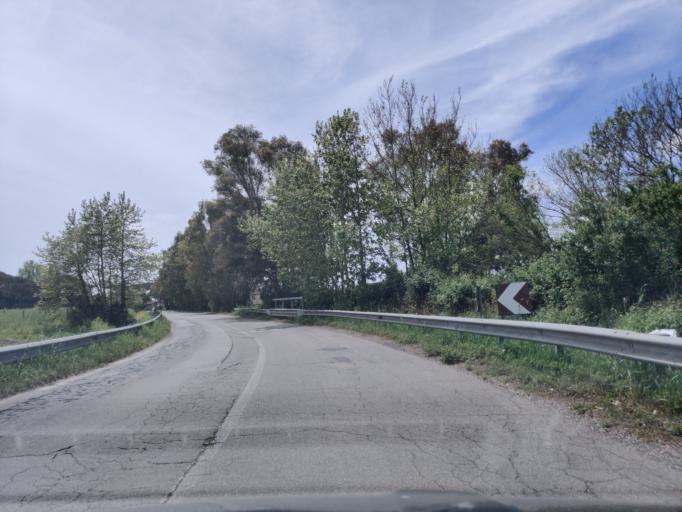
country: IT
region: Latium
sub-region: Citta metropolitana di Roma Capitale
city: Maccarese
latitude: 41.8802
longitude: 12.2141
